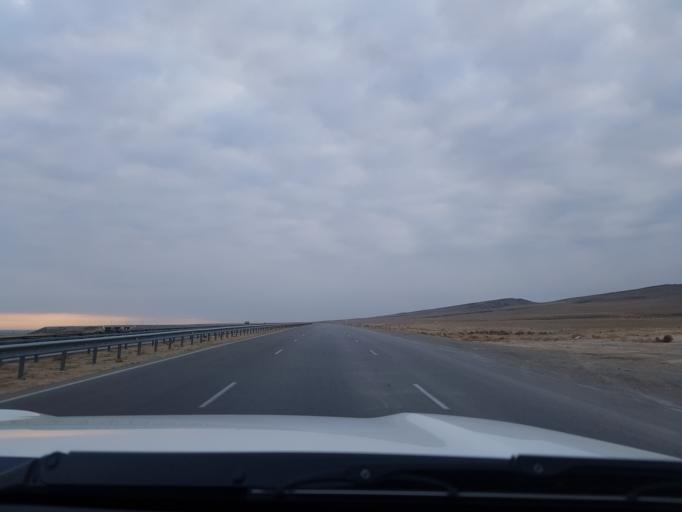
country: IR
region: Razavi Khorasan
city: Dargaz
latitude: 37.6843
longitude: 59.0698
